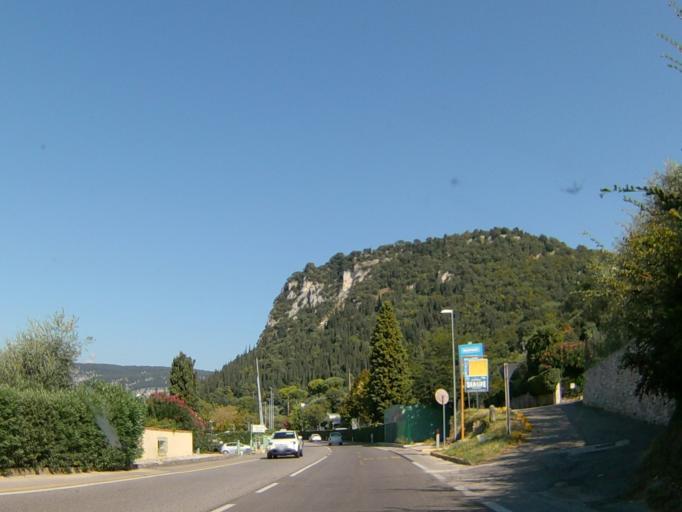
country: IT
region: Veneto
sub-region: Provincia di Verona
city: Garda
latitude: 45.5629
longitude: 10.7146
